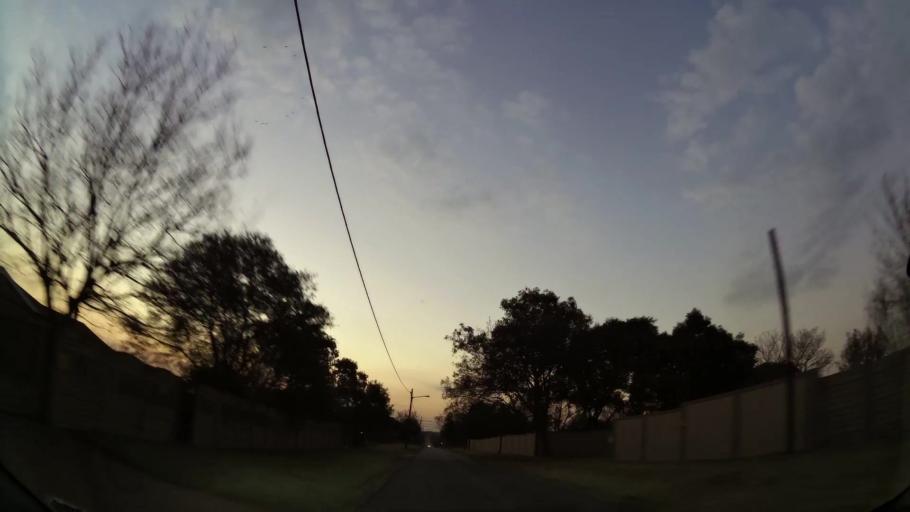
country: ZA
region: Gauteng
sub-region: Ekurhuleni Metropolitan Municipality
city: Benoni
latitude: -26.1320
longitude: 28.3118
